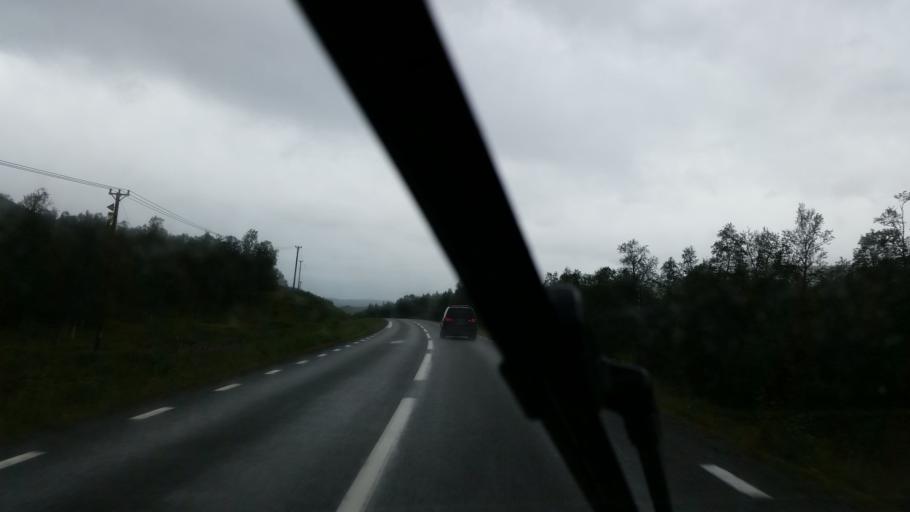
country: NO
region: Nordland
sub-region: Rana
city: Mo i Rana
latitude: 65.9103
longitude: 14.9894
